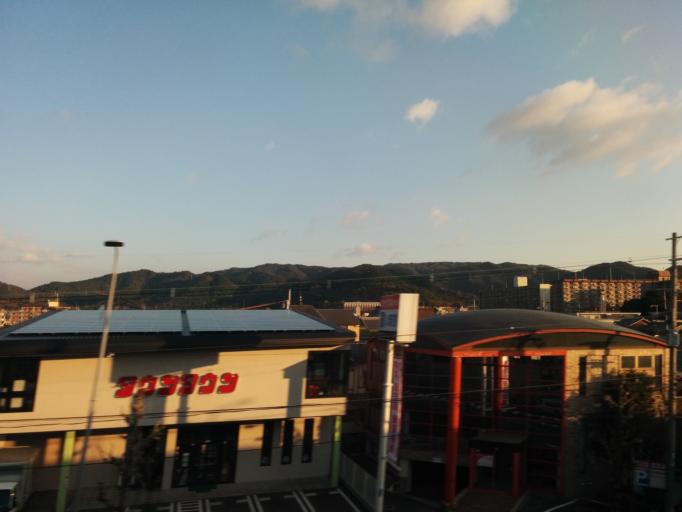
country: JP
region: Kyoto
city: Kyoto
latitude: 34.9813
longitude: 135.8064
